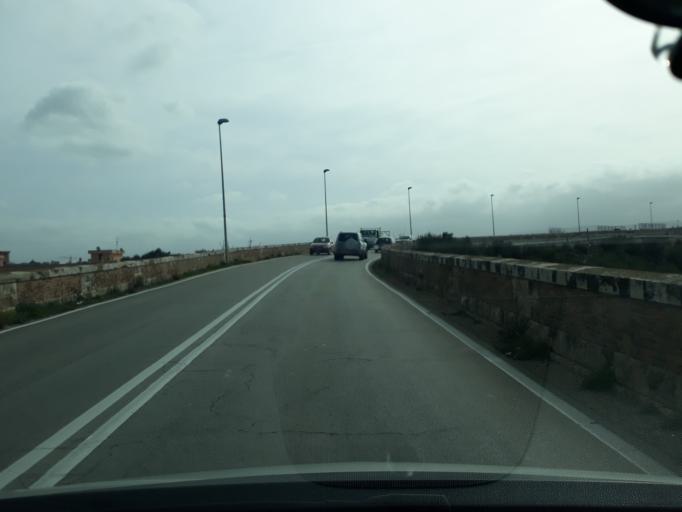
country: IT
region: Apulia
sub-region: Provincia di Bari
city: Monopoli
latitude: 40.9582
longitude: 17.2825
